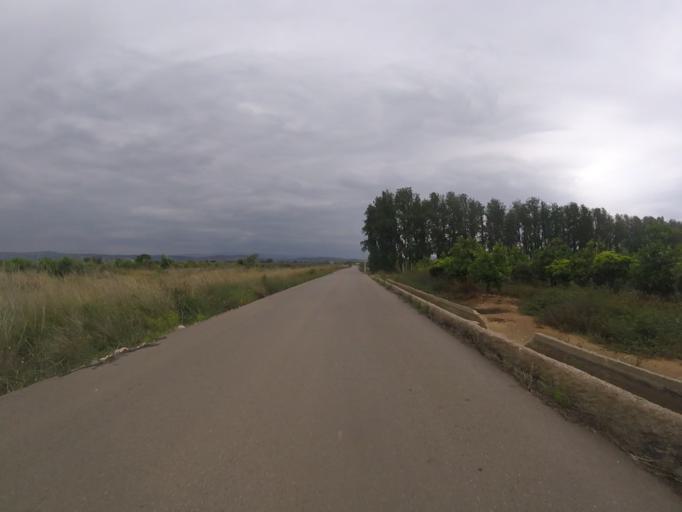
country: ES
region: Valencia
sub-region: Provincia de Castello
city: Alcoceber
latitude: 40.2111
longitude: 0.2505
